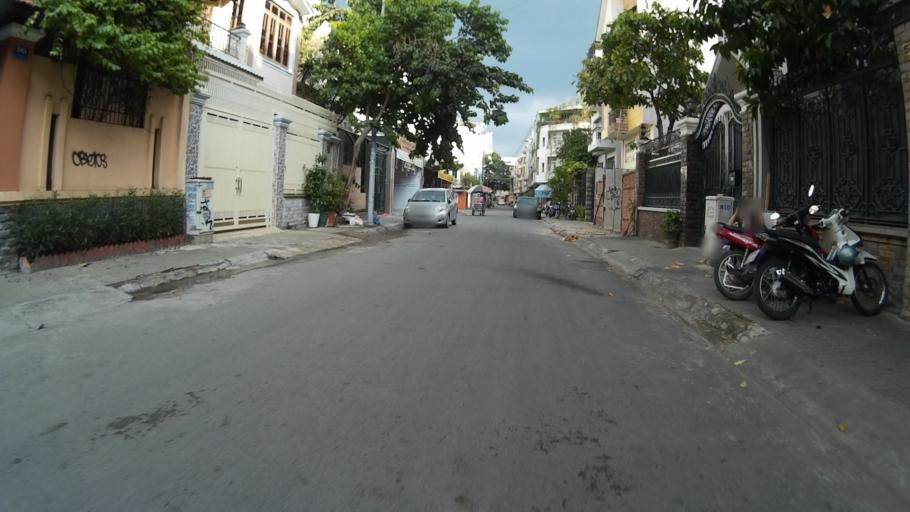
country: VN
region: Ho Chi Minh City
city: Quan Binh Thanh
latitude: 10.7968
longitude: 106.6875
